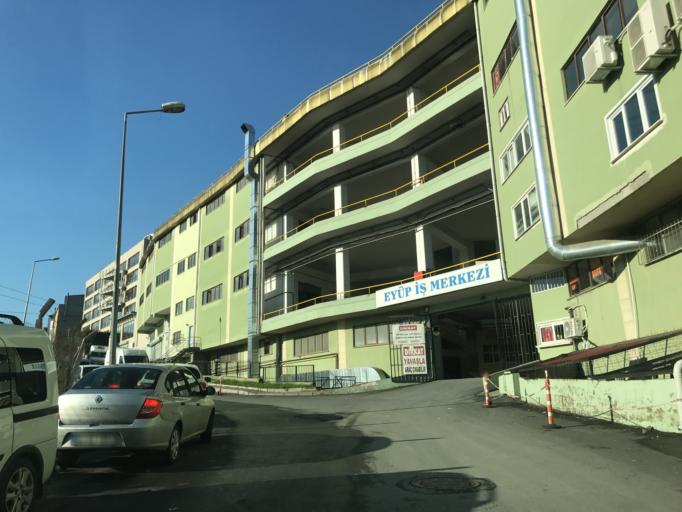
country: TR
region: Istanbul
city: Istanbul
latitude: 41.0370
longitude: 28.9333
